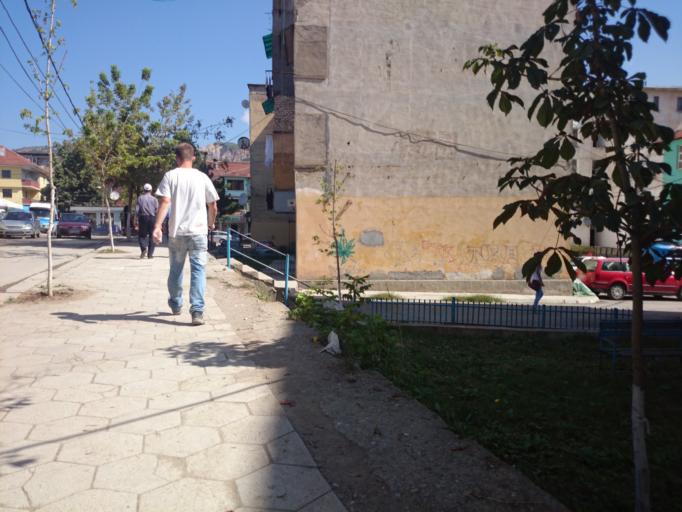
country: AL
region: Diber
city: Peshkopi
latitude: 41.6834
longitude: 20.4261
